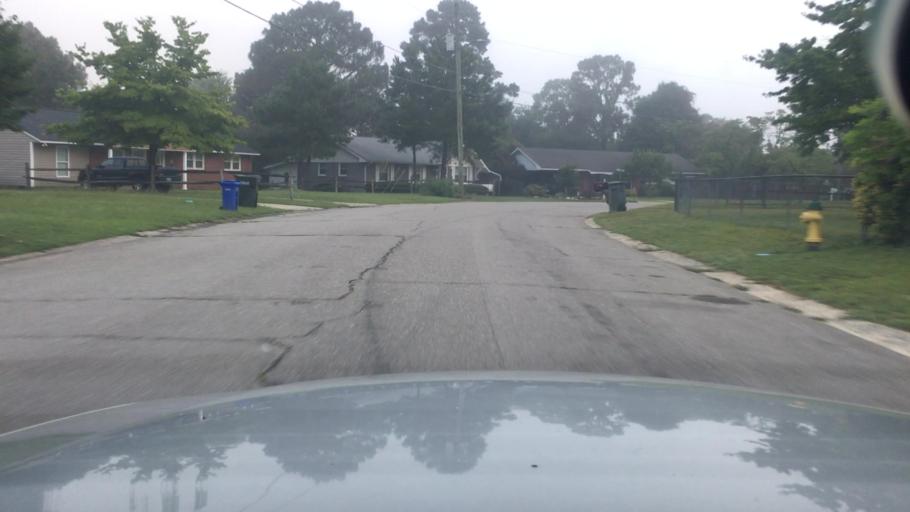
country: US
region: North Carolina
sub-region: Cumberland County
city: Hope Mills
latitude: 35.0213
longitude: -78.9452
